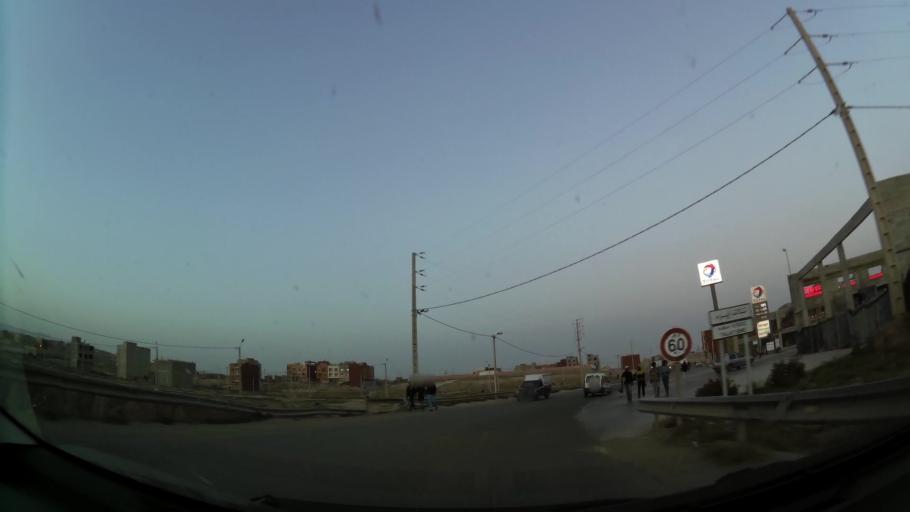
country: MA
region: Souss-Massa-Draa
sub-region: Inezgane-Ait Mellou
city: Inezgane
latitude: 30.3759
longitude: -9.4881
